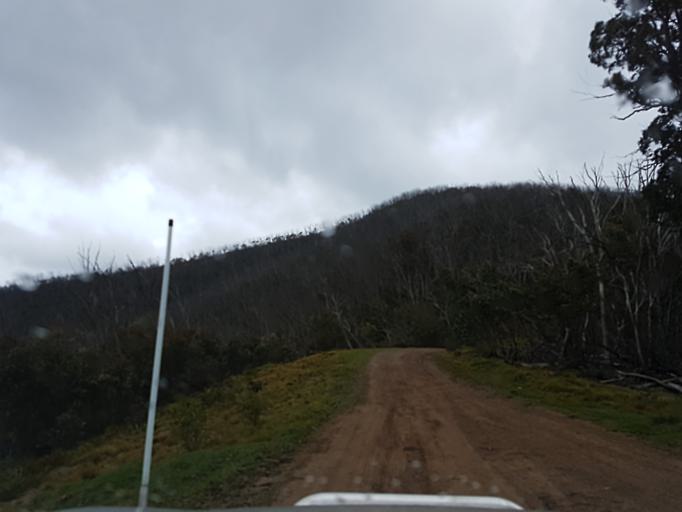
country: AU
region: Victoria
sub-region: Alpine
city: Mount Beauty
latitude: -37.0918
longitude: 147.0959
